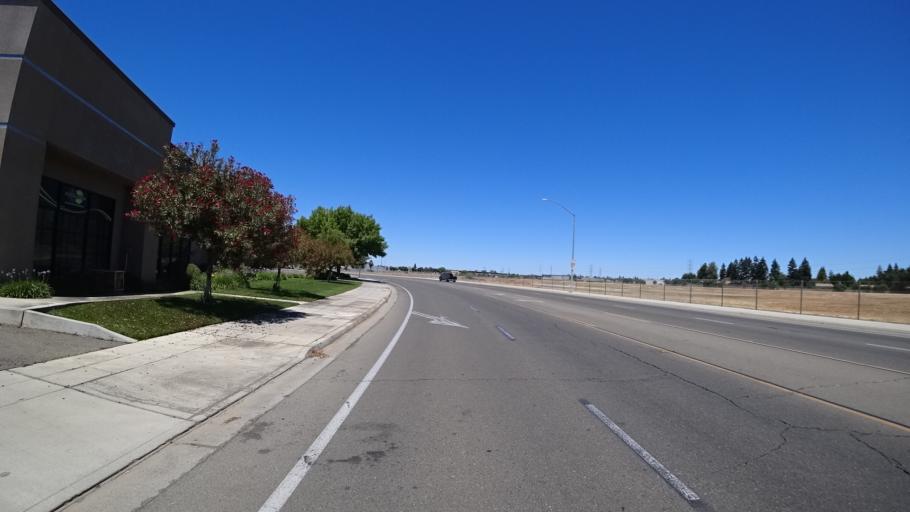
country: US
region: California
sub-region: Fresno County
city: West Park
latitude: 36.8023
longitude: -119.8547
